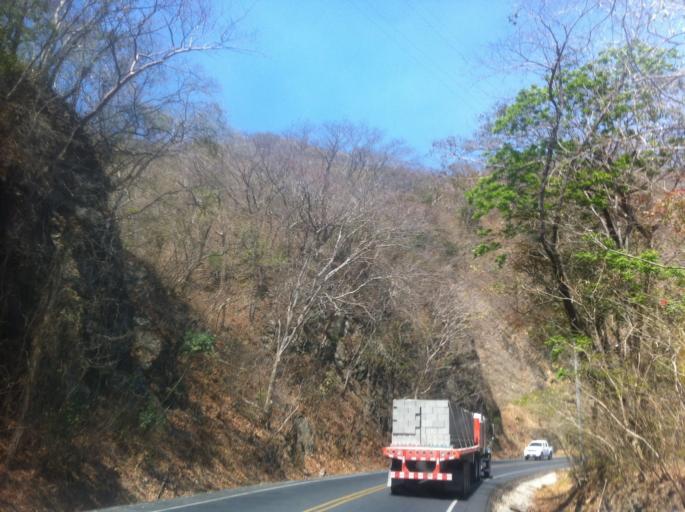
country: CR
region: Guanacaste
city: Santa Cruz
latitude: 10.2178
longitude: -85.5155
